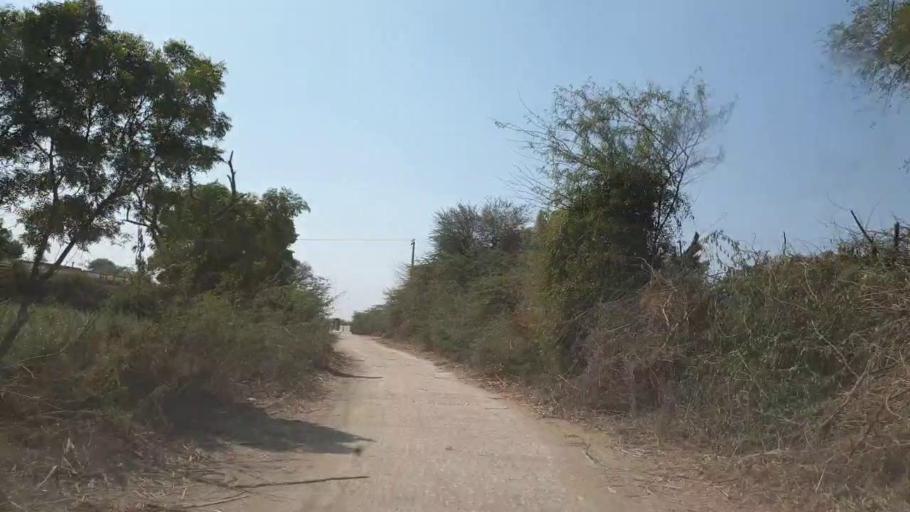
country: PK
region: Sindh
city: Mirpur Khas
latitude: 25.7362
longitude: 69.0770
